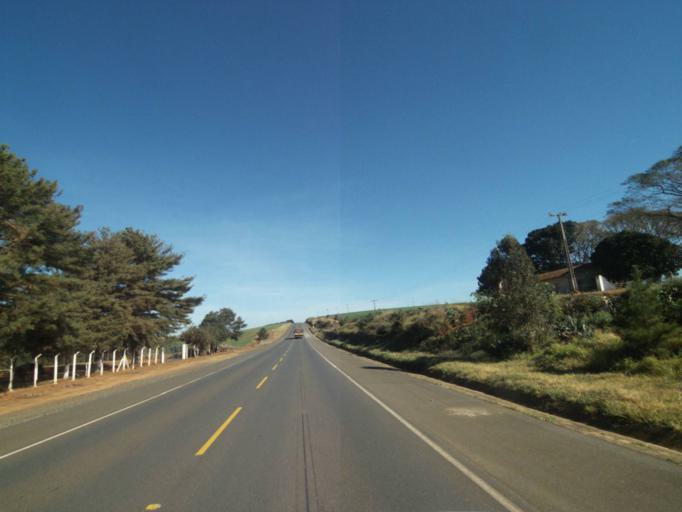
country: BR
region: Parana
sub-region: Tibagi
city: Tibagi
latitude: -24.3588
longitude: -50.3190
